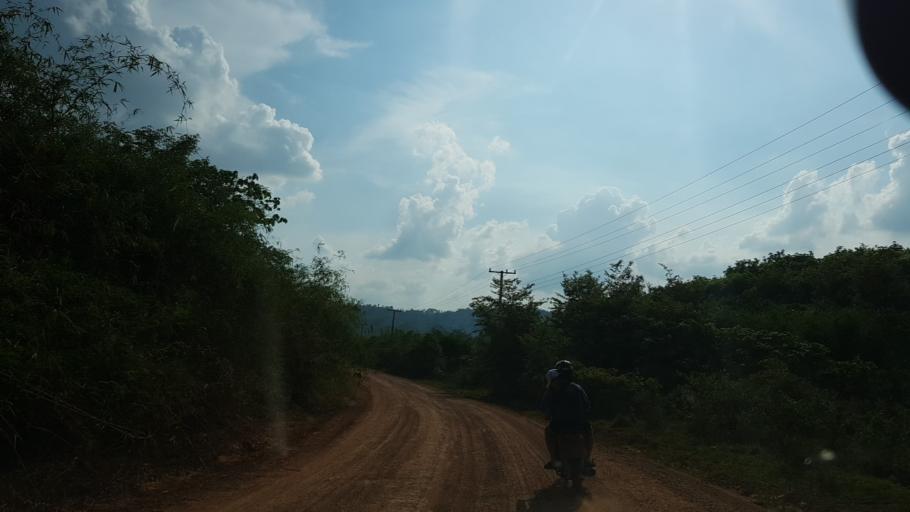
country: LA
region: Vientiane
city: Muang Phon-Hong
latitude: 18.3523
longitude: 102.2783
